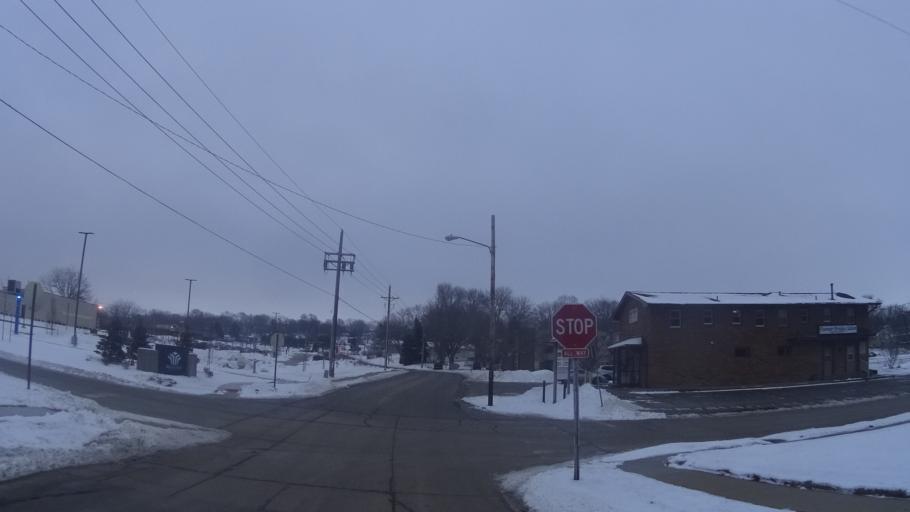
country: US
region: Nebraska
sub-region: Sarpy County
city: Offutt Air Force Base
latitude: 41.1488
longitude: -95.9193
